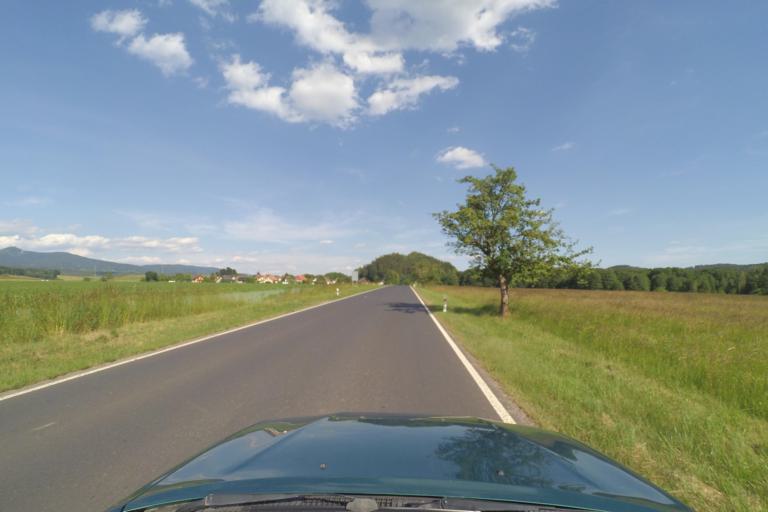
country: CZ
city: Osecna
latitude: 50.6993
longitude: 14.8984
